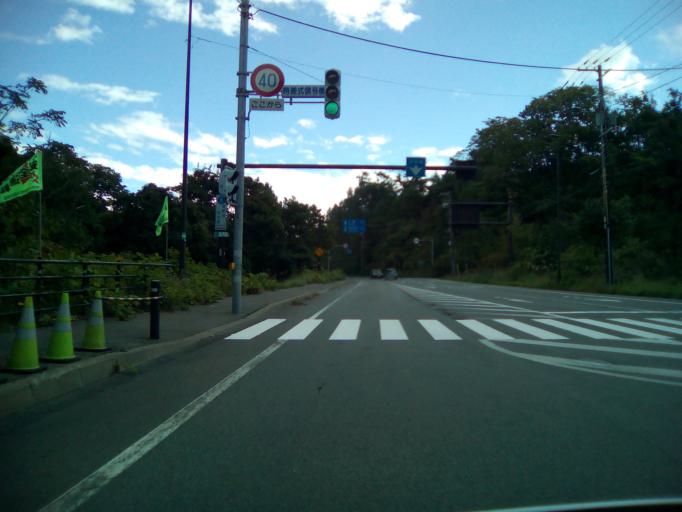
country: JP
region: Hokkaido
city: Date
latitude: 42.5708
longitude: 140.7997
